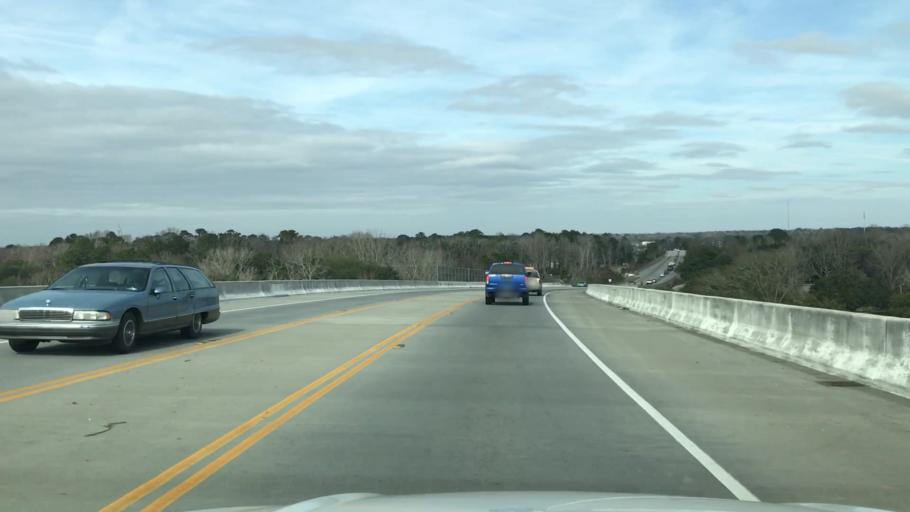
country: US
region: South Carolina
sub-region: Charleston County
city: Shell Point
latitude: 32.7868
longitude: -80.1079
